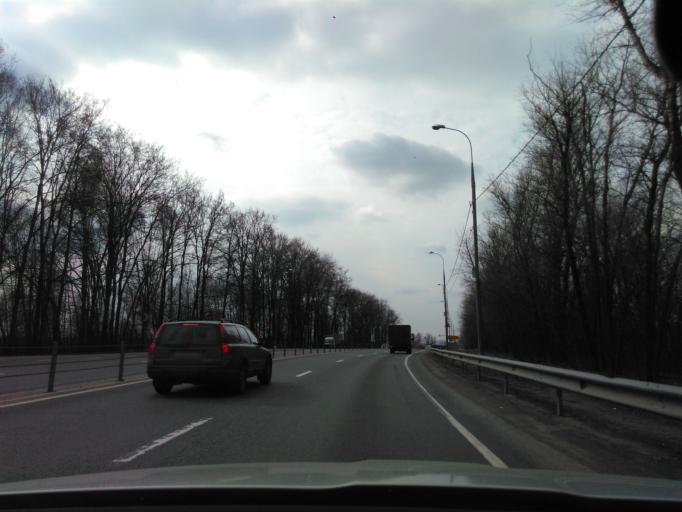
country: RU
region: Moskovskaya
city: Marfino
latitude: 56.0140
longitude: 37.5463
